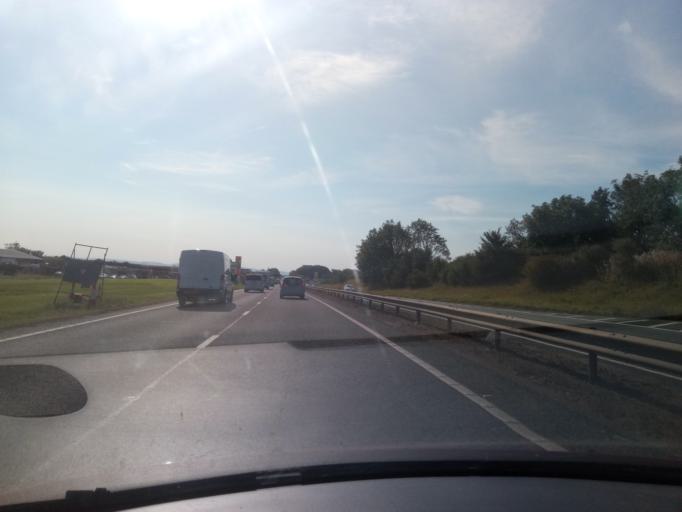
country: GB
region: England
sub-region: Hartlepool
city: Elwick
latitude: 54.6577
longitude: -1.3040
